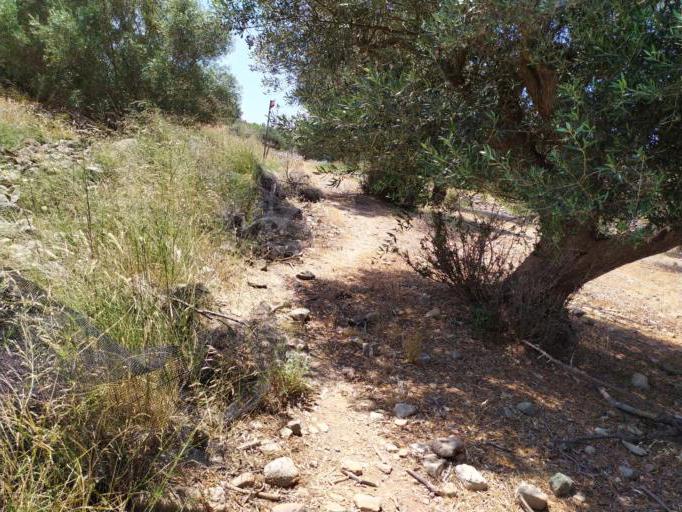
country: GR
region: Crete
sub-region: Nomos Irakleiou
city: Agioi Deka
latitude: 35.0597
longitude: 24.9504
